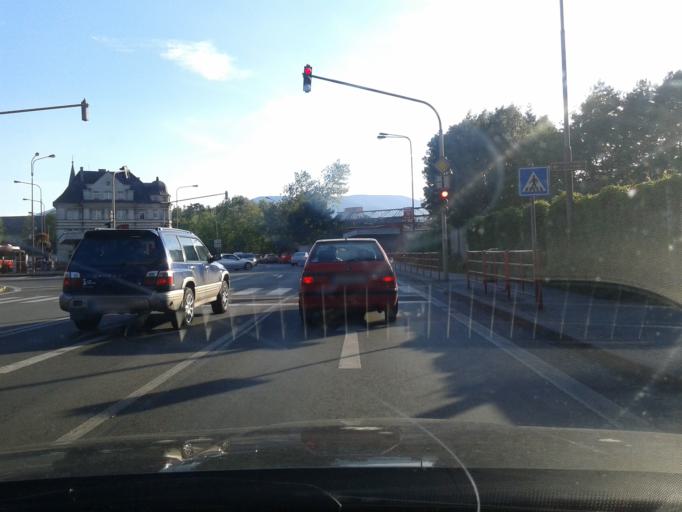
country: CZ
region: Moravskoslezsky
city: Trinec
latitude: 49.6815
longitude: 18.6666
